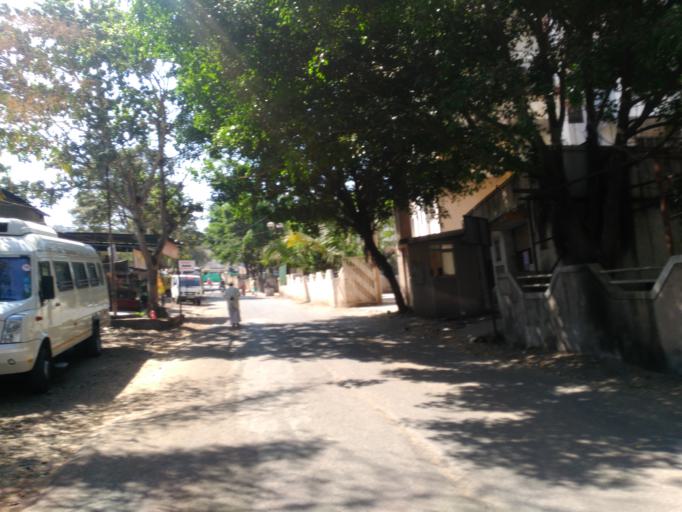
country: IN
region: Maharashtra
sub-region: Pune Division
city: Pune
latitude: 18.4489
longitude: 73.8763
